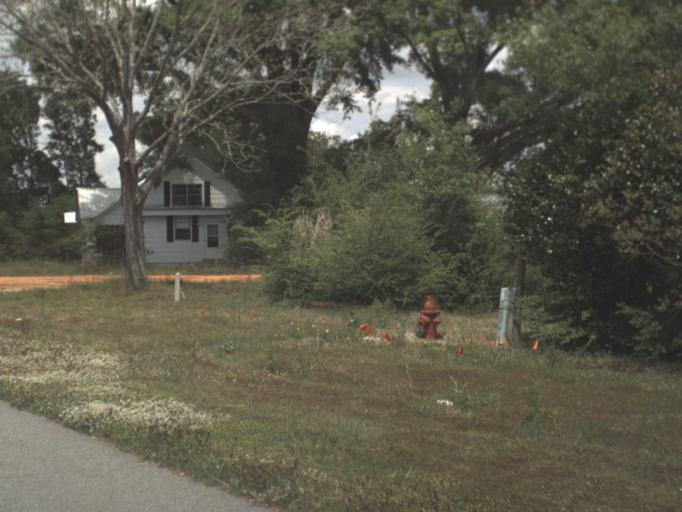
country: US
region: Alabama
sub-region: Escambia County
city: Atmore
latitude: 30.9706
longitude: -87.4873
